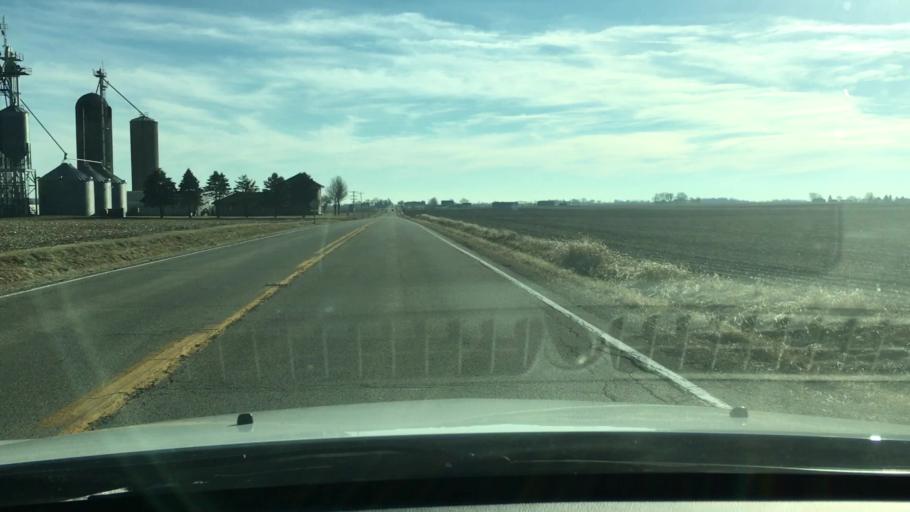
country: US
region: Illinois
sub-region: LaSalle County
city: Mendota
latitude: 41.4973
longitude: -89.1272
